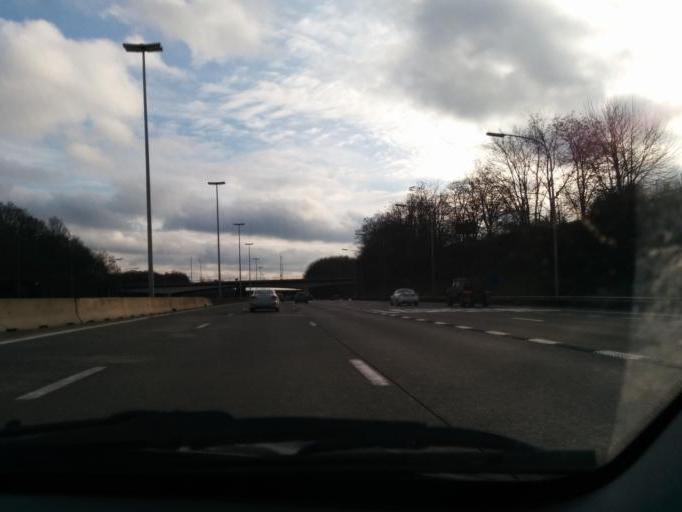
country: BE
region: Flanders
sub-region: Provincie Vlaams-Brabant
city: Kraainem
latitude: 50.8733
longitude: 4.4658
